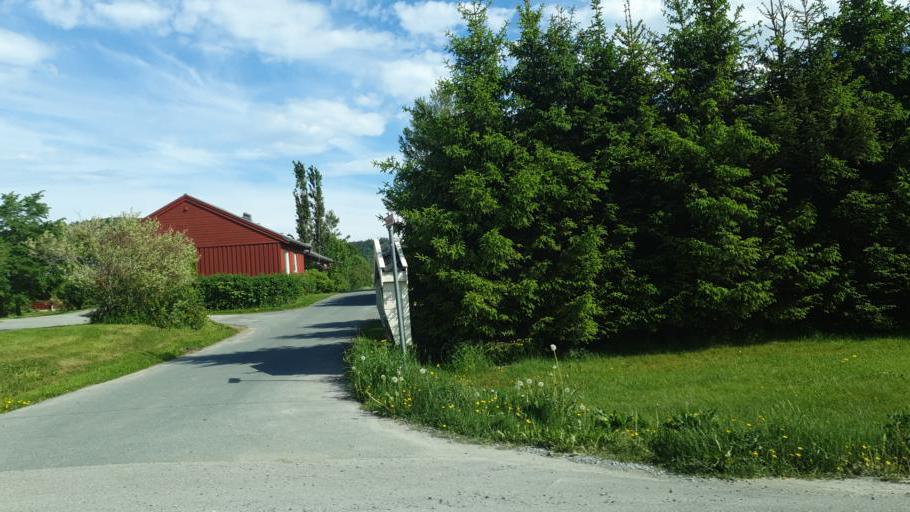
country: NO
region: Sor-Trondelag
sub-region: Rissa
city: Rissa
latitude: 63.5077
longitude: 10.0162
